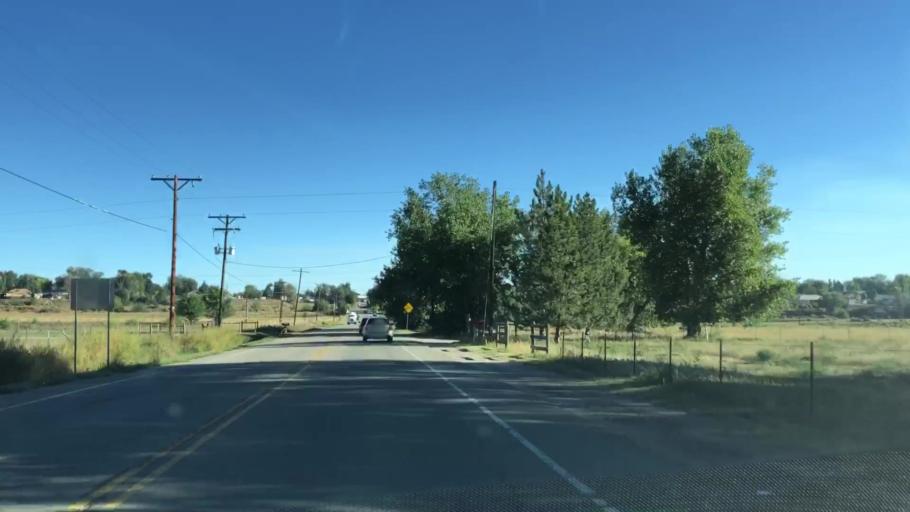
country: US
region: Colorado
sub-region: Larimer County
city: Loveland
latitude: 40.4015
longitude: -105.1228
